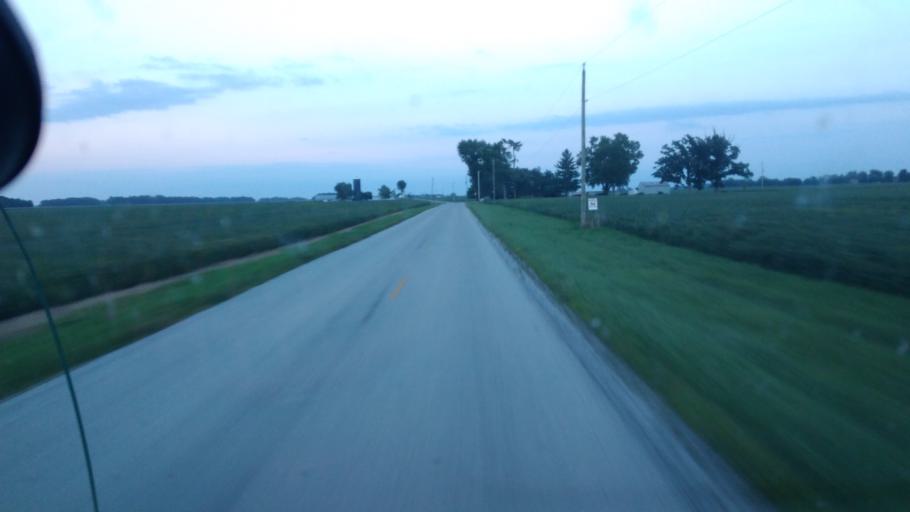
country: US
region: Ohio
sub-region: Hardin County
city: Kenton
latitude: 40.6722
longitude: -83.4805
